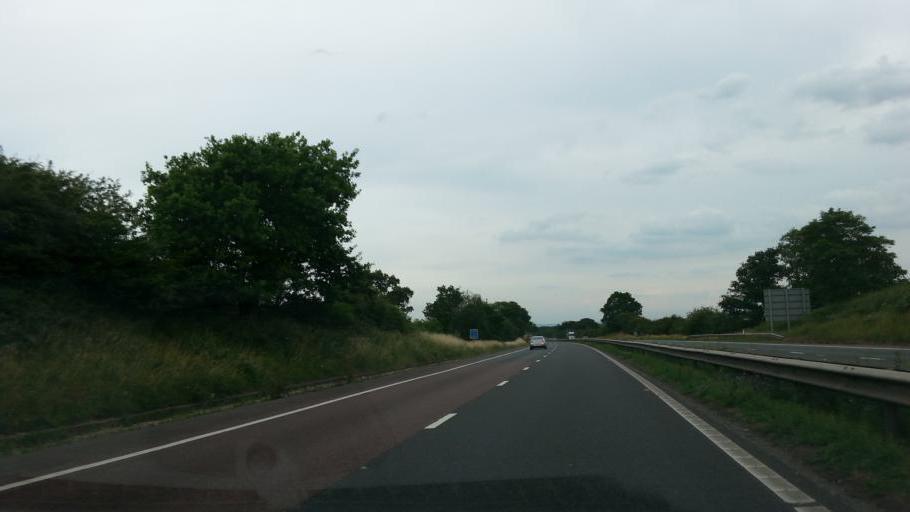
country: GB
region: England
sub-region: Herefordshire
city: Donnington
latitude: 51.9947
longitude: -2.3446
